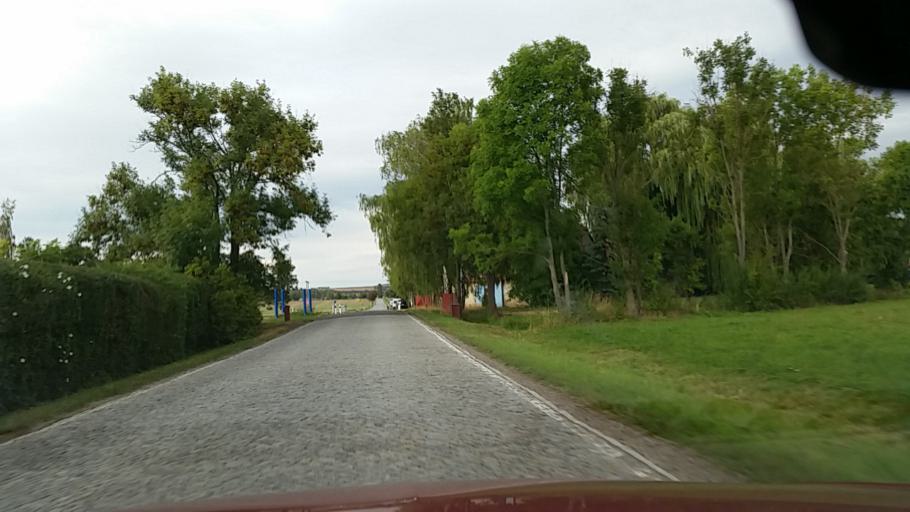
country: DE
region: Thuringia
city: Kolleda
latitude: 51.1943
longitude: 11.2531
